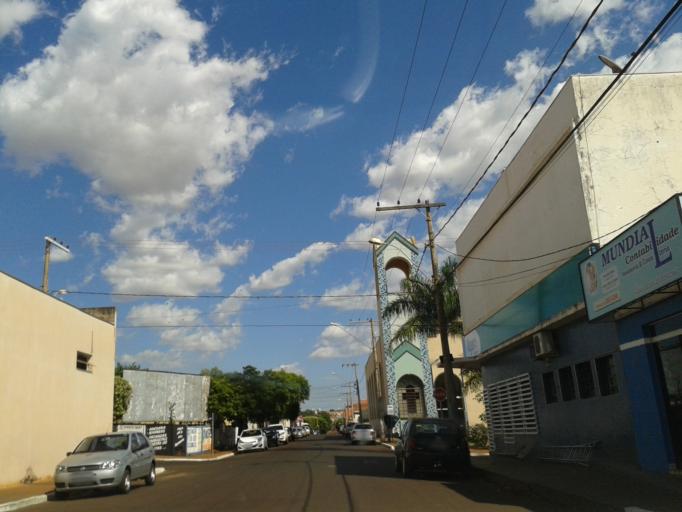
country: BR
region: Minas Gerais
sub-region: Capinopolis
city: Capinopolis
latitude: -18.6813
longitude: -49.5709
